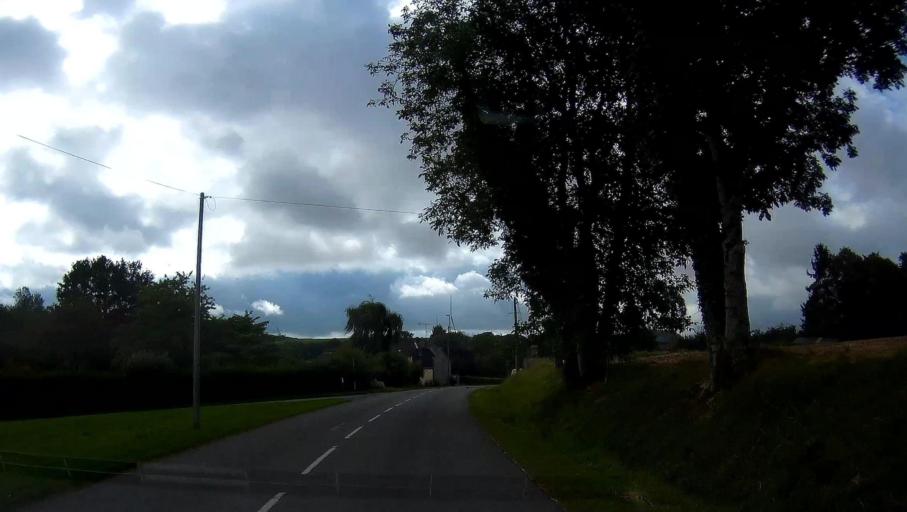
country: FR
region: Champagne-Ardenne
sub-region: Departement des Ardennes
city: Chateau-Porcien
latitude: 49.6121
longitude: 4.2343
